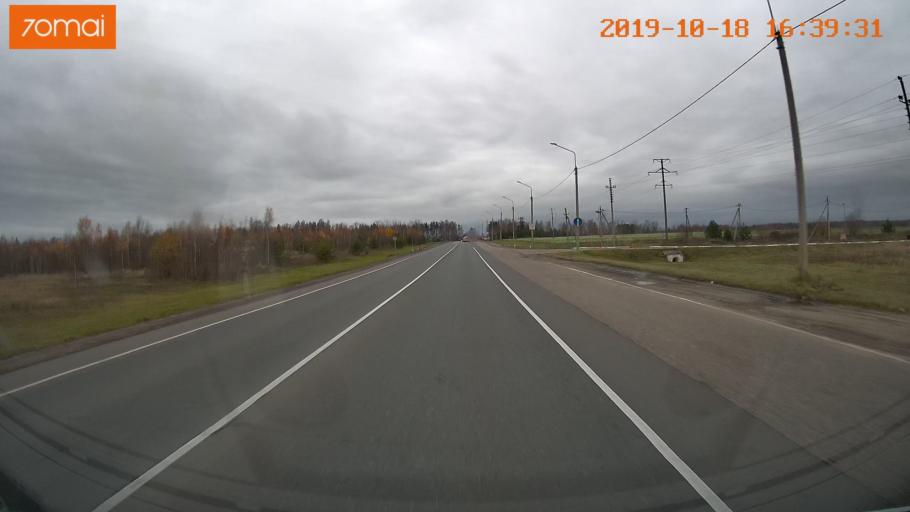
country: RU
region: Vladimir
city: Suzdal'
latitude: 56.4527
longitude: 40.4623
